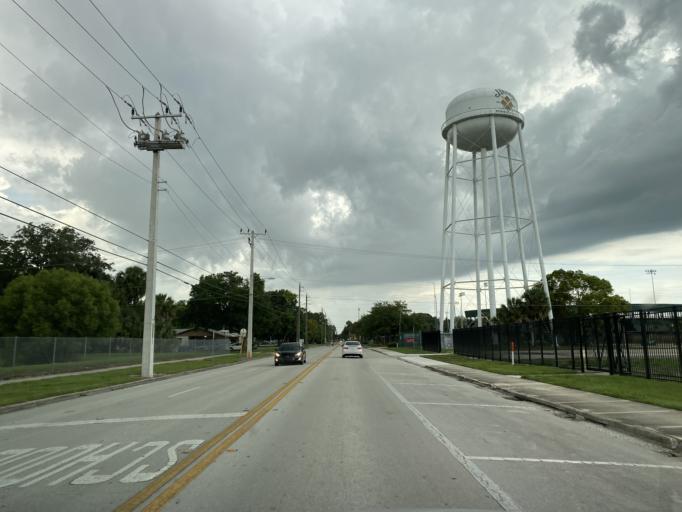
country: US
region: Florida
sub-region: Seminole County
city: Sanford
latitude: 28.8020
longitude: -81.2556
